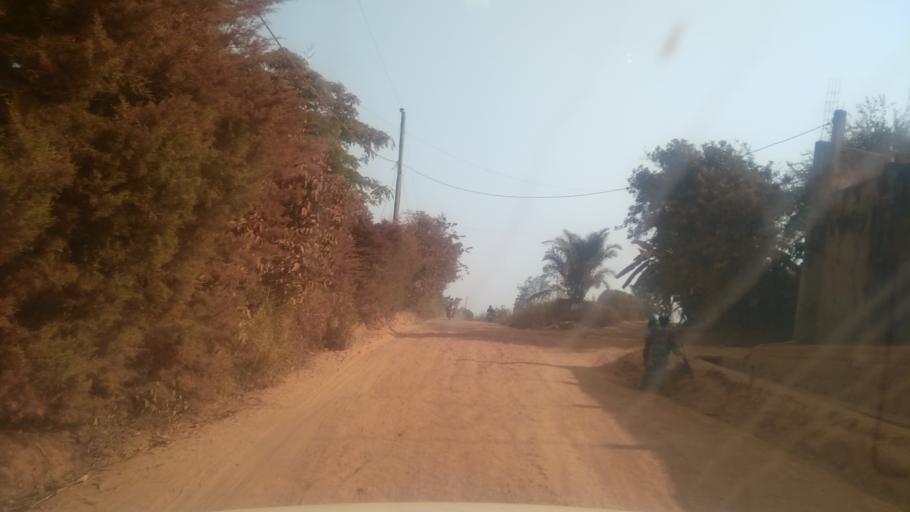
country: CM
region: West
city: Bafoussam
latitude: 5.5169
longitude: 10.4100
